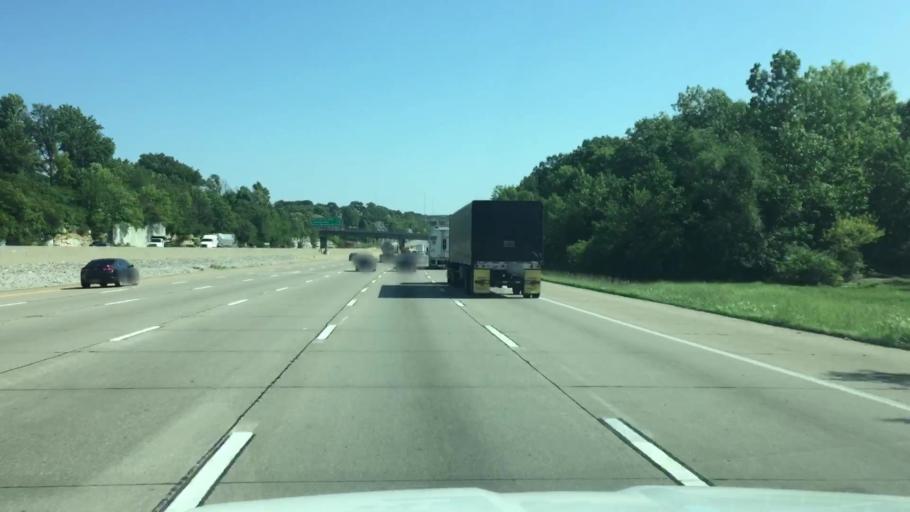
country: US
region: Missouri
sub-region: Saint Louis County
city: Mehlville
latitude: 38.4925
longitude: -90.3496
